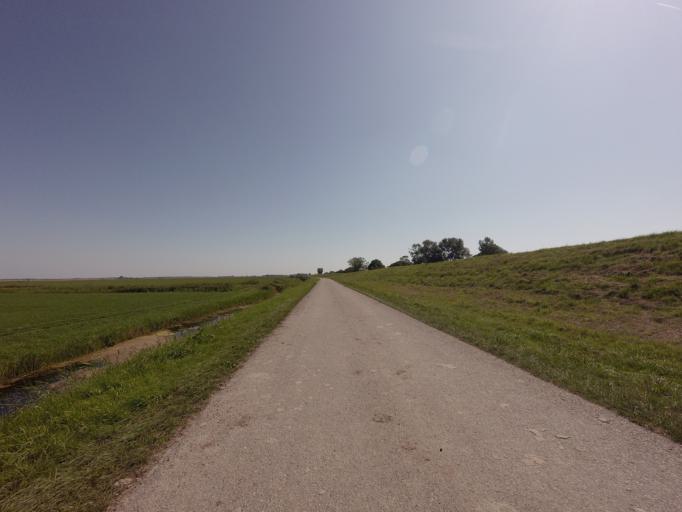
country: NL
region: Friesland
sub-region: Gemeente Dongeradeel
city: Anjum
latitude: 53.3935
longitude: 6.1139
